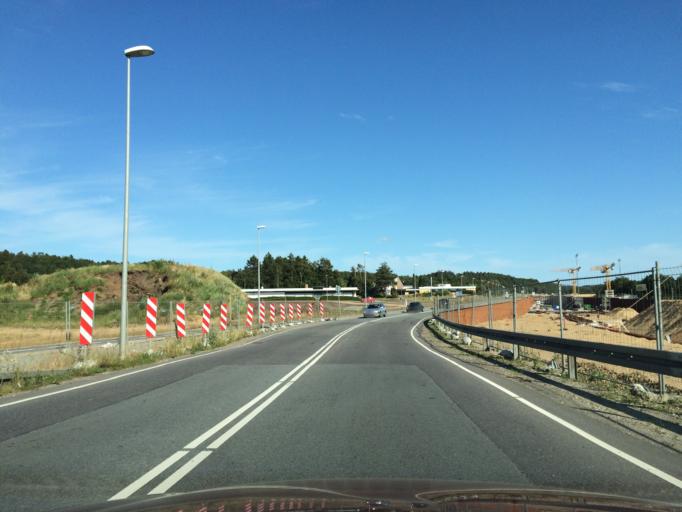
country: DK
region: Central Jutland
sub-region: Silkeborg Kommune
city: Silkeborg
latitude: 56.1844
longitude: 9.5799
